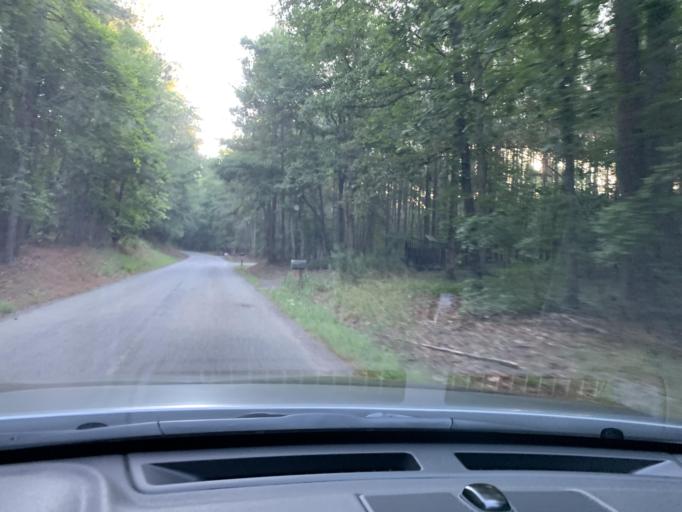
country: US
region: Georgia
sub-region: Bartow County
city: Rydal
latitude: 34.2292
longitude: -84.6474
